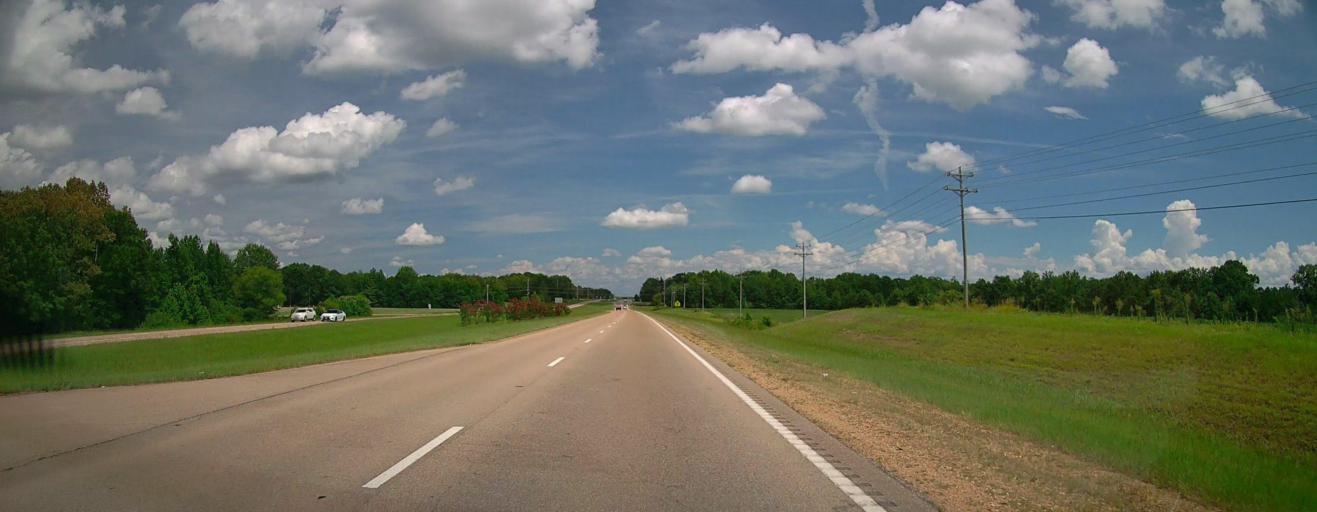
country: US
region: Mississippi
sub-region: Lee County
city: Shannon
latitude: 34.1117
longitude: -88.6883
